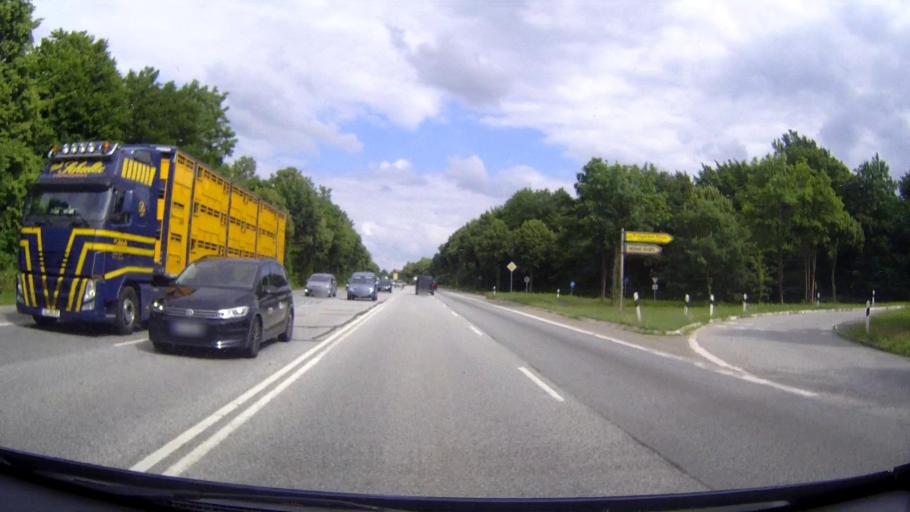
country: DE
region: Schleswig-Holstein
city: Bad Segeberg
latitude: 53.9365
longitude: 10.2958
